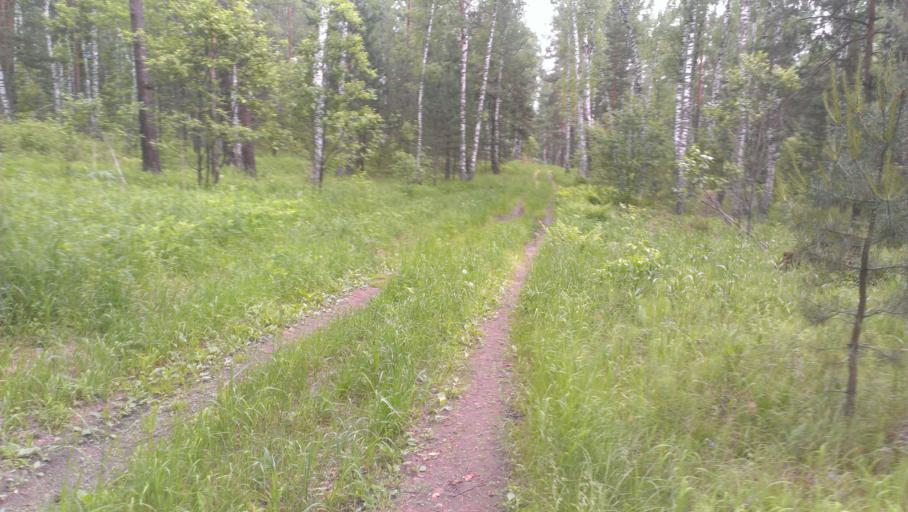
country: RU
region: Altai Krai
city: Sannikovo
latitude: 53.3462
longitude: 84.0414
